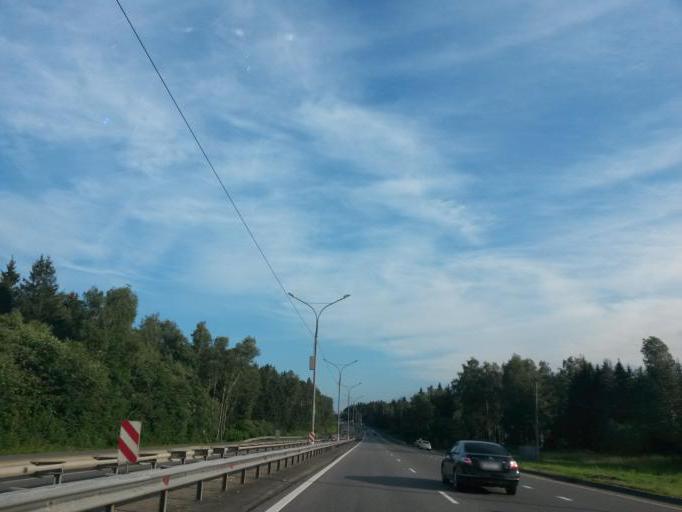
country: RU
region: Moskovskaya
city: Vostryakovo
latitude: 55.4643
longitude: 37.8538
